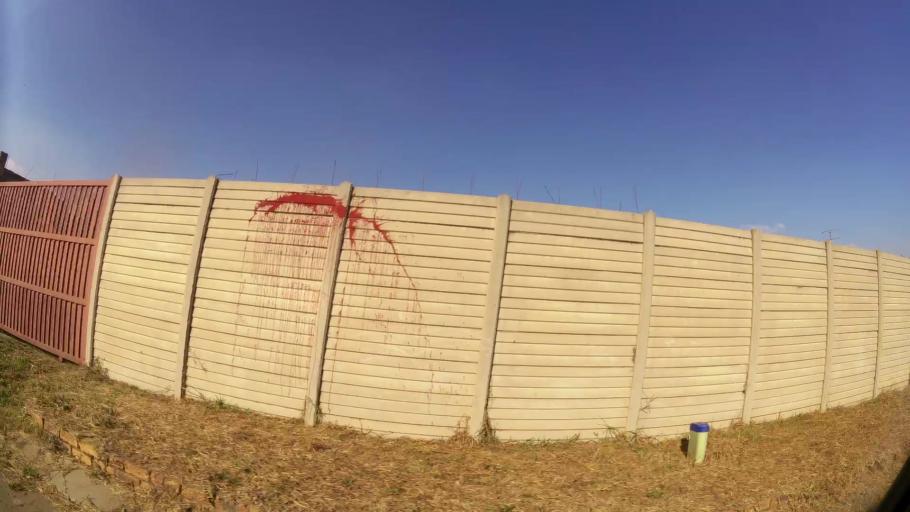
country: ZA
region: Gauteng
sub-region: Ekurhuleni Metropolitan Municipality
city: Brakpan
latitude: -26.2201
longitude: 28.3607
